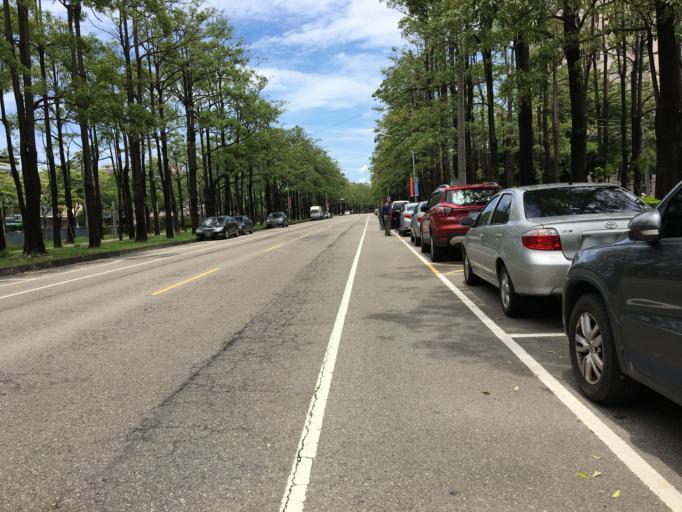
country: TW
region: Taiwan
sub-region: Taichung City
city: Taichung
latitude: 24.1207
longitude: 120.6719
